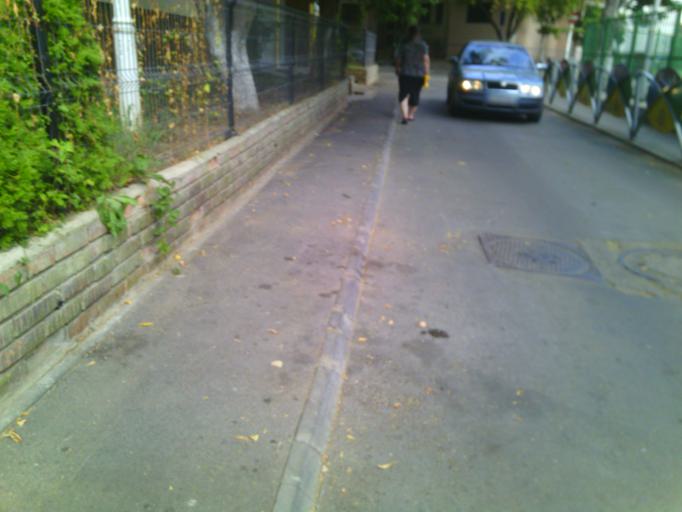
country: RO
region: Bucuresti
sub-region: Municipiul Bucuresti
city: Bucuresti
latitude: 44.3794
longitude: 26.0973
